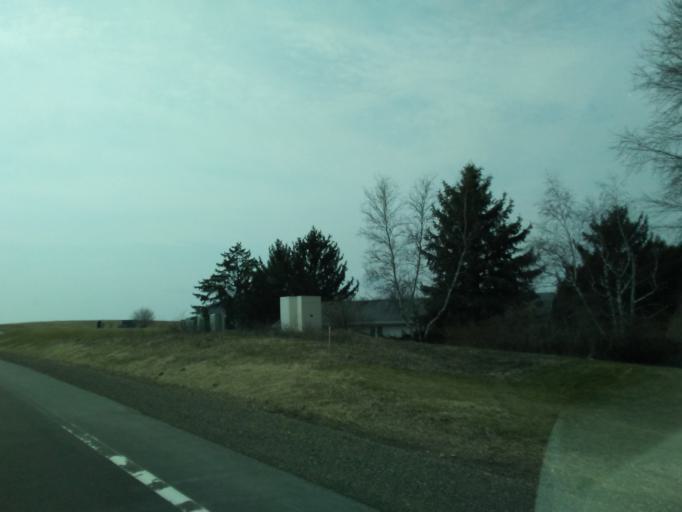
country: US
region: Wisconsin
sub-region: Dane County
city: Waunakee
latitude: 43.1786
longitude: -89.4619
